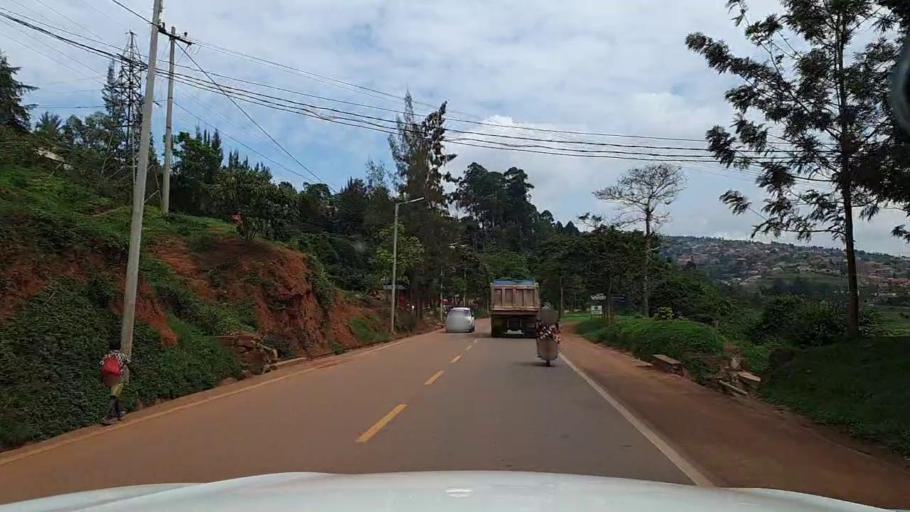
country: RW
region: Kigali
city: Kigali
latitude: -1.9107
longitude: 30.0477
